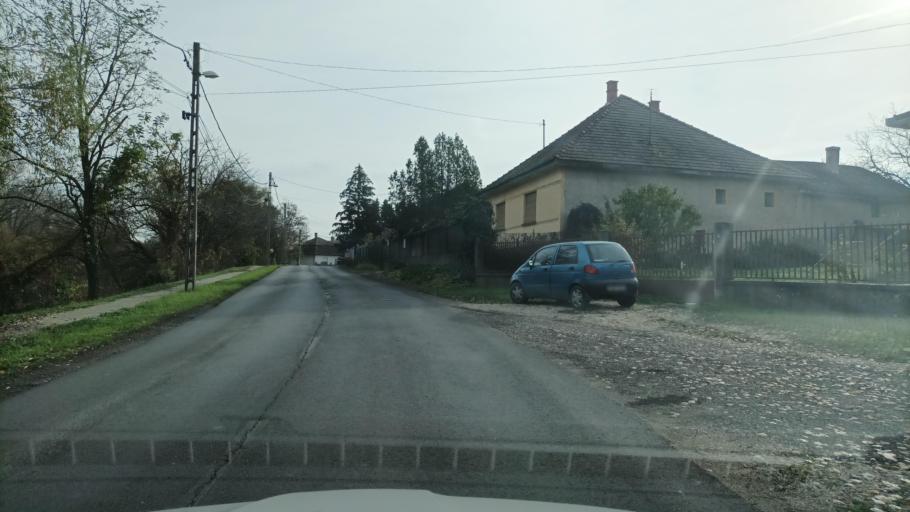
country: HU
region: Pest
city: Rackeve
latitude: 47.1381
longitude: 18.9470
